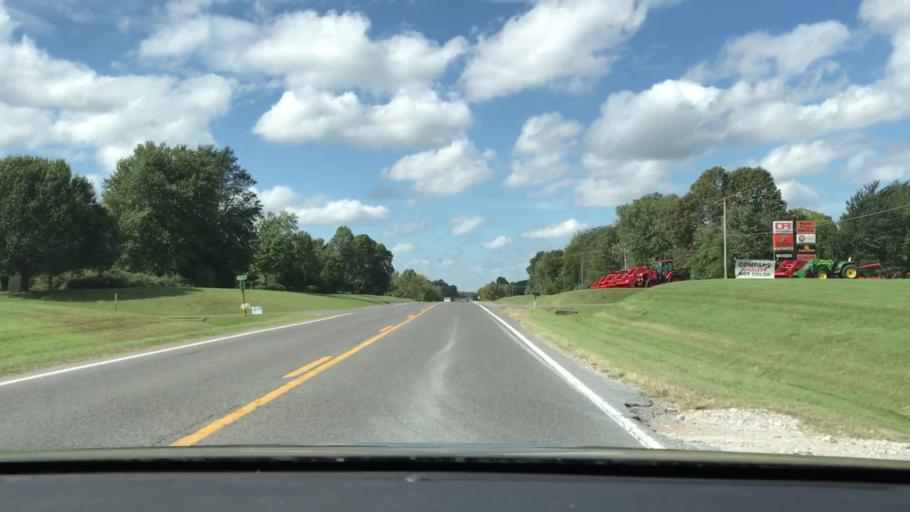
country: US
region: Kentucky
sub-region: Livingston County
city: Ledbetter
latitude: 37.0069
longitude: -88.4635
